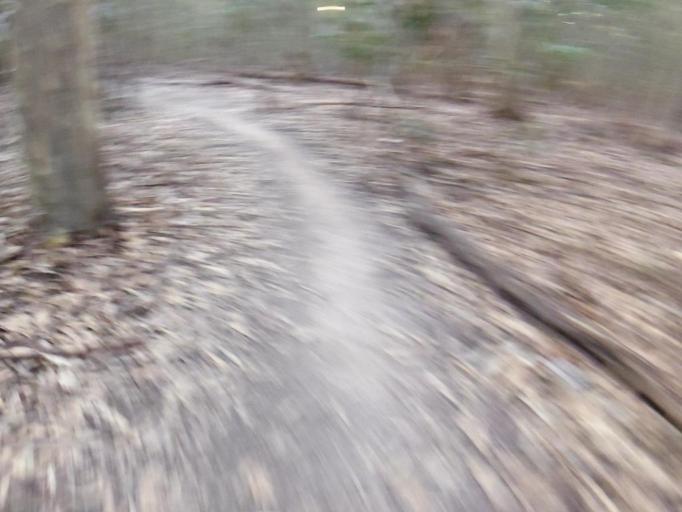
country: AU
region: Victoria
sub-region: Yarra Ranges
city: Lysterfield
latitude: -37.9485
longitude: 145.3036
